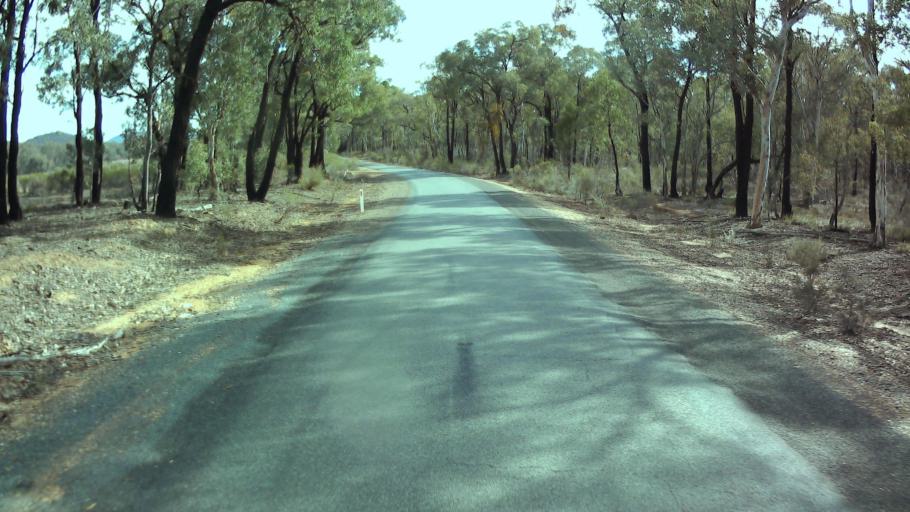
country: AU
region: New South Wales
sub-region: Weddin
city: Grenfell
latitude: -33.8631
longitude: 148.2130
